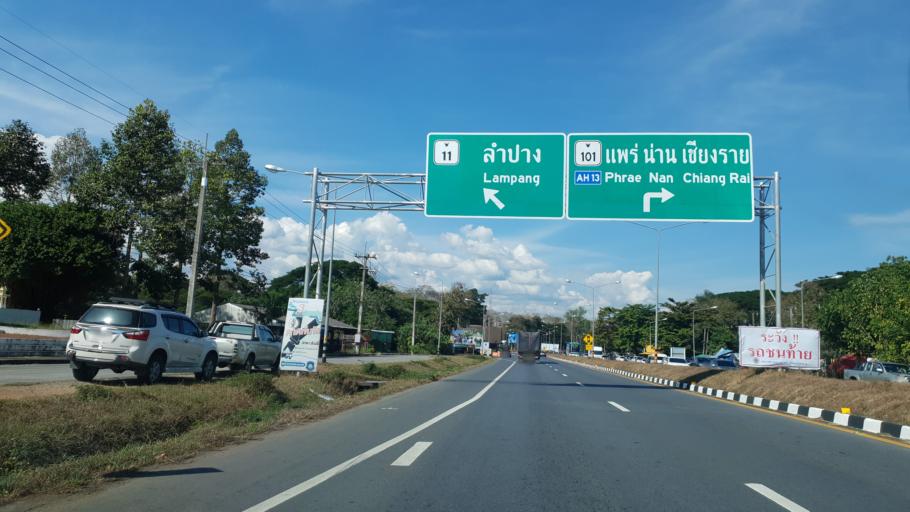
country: TH
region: Phrae
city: Den Chai
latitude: 17.9657
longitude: 100.0662
